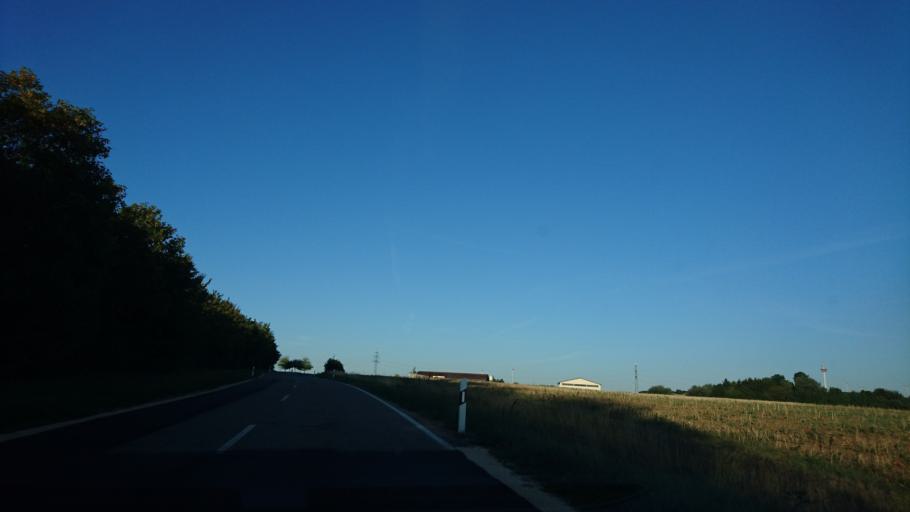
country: DE
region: Bavaria
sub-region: Regierungsbezirk Mittelfranken
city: Nennslingen
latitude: 49.0442
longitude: 11.1245
